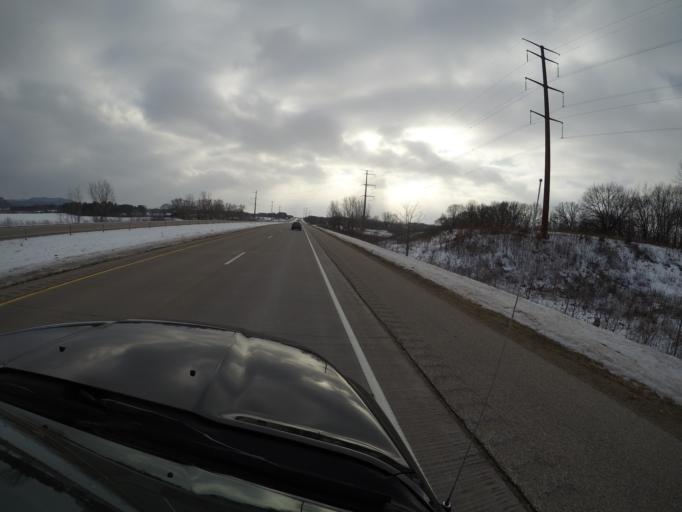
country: US
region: Wisconsin
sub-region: La Crosse County
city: Holmen
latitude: 43.9837
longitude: -91.2864
